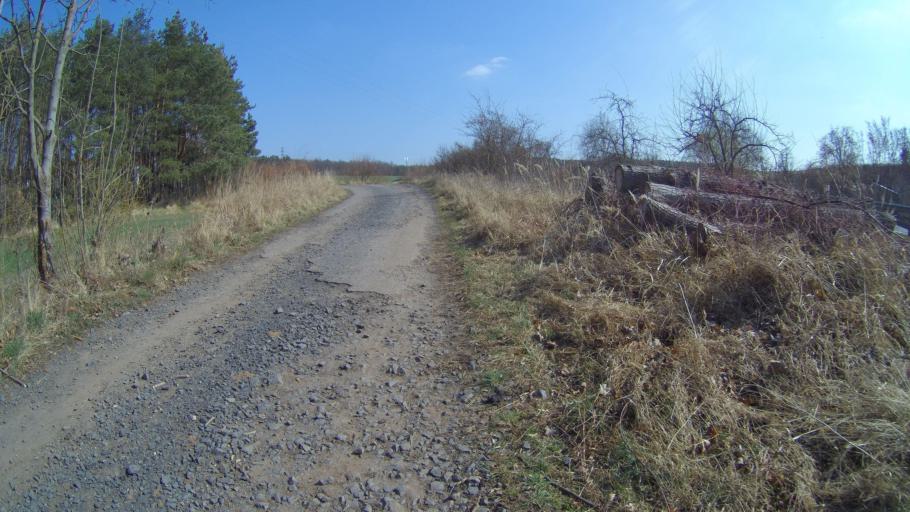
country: CZ
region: Ustecky
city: Mecholupy
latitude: 50.2759
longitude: 13.5696
